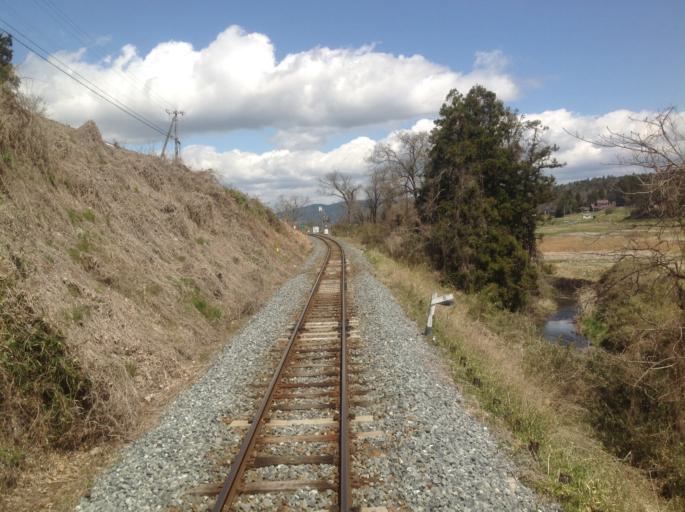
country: JP
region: Iwate
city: Ichinoseki
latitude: 38.9106
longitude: 141.1777
